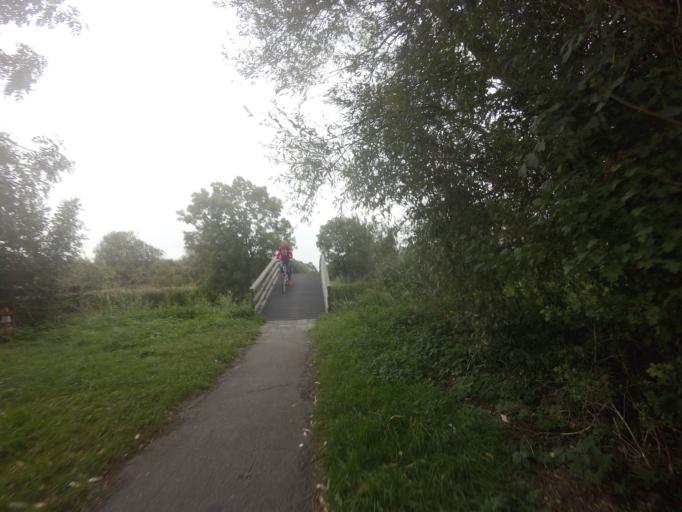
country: NL
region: Friesland
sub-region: Gemeente Leeuwarden
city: Bilgaard
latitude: 53.2258
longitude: 5.7925
